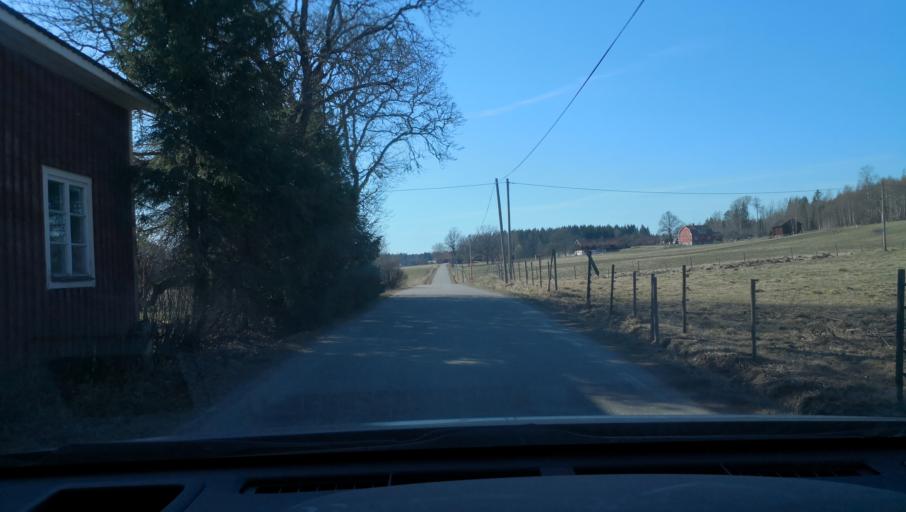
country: SE
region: Vaestmanland
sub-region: Sala Kommun
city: Sala
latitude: 60.0785
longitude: 16.4690
